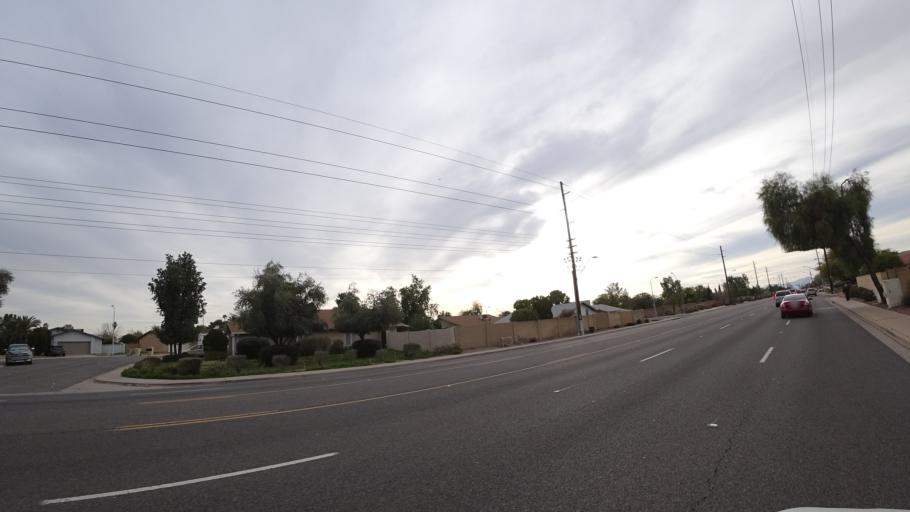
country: US
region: Arizona
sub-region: Maricopa County
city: Glendale
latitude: 33.5676
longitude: -112.1810
